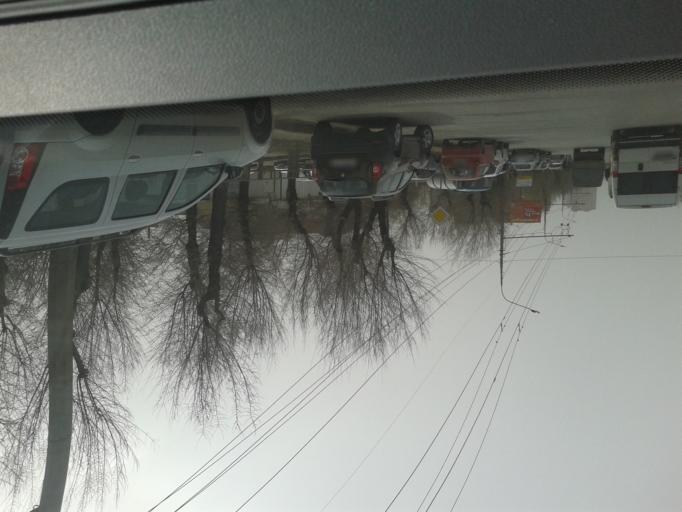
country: RU
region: Volgograd
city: Volgograd
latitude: 48.7322
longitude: 44.4964
